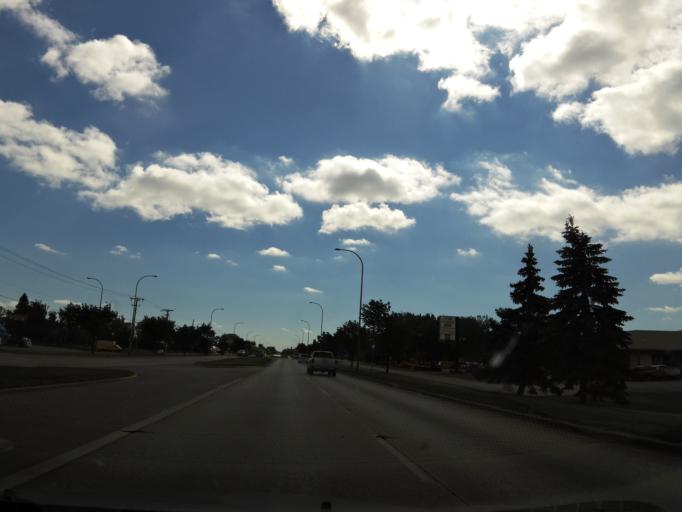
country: US
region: North Dakota
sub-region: Grand Forks County
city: Grand Forks
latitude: 47.9330
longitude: -97.0797
